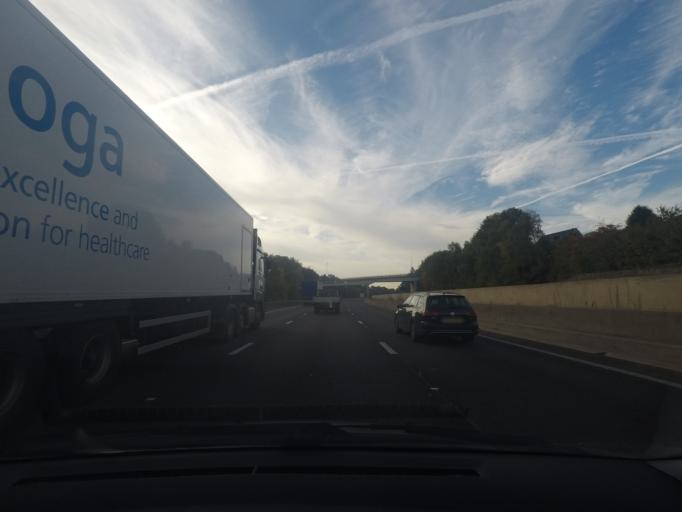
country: GB
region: England
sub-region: Barnsley
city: Darton
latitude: 53.5852
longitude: -1.5354
